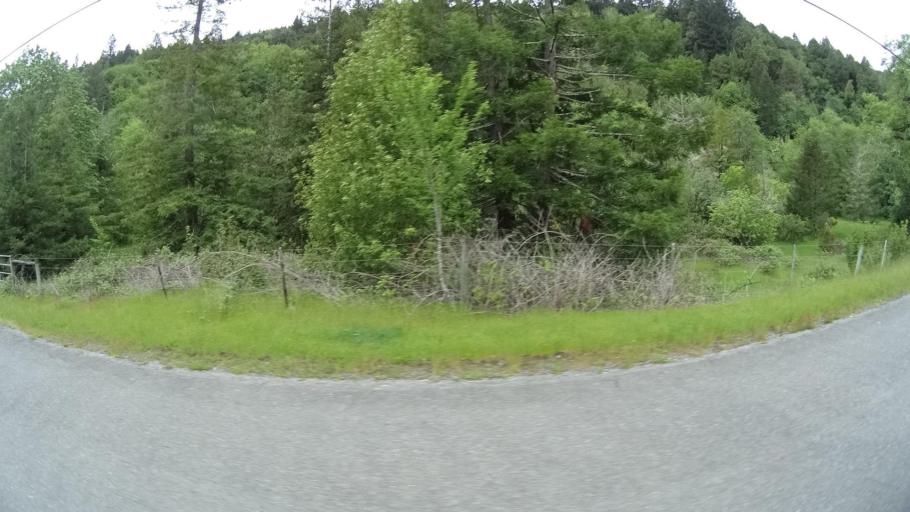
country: US
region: California
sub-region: Humboldt County
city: Blue Lake
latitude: 40.9652
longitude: -123.8418
